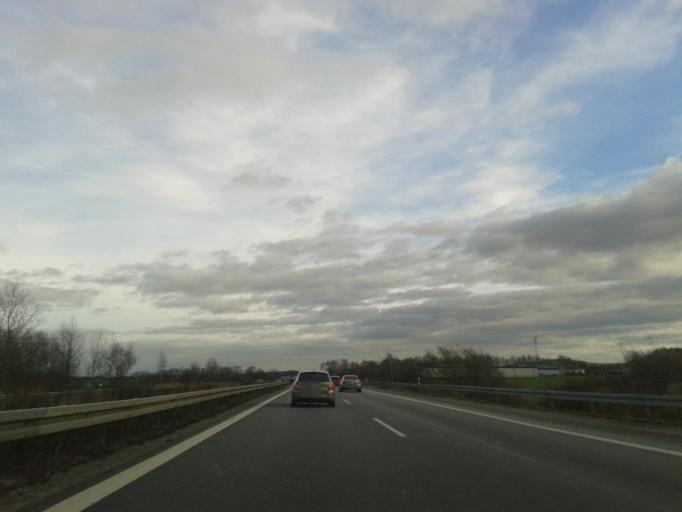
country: DE
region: Saxony
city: Burkau
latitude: 51.1822
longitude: 14.1587
